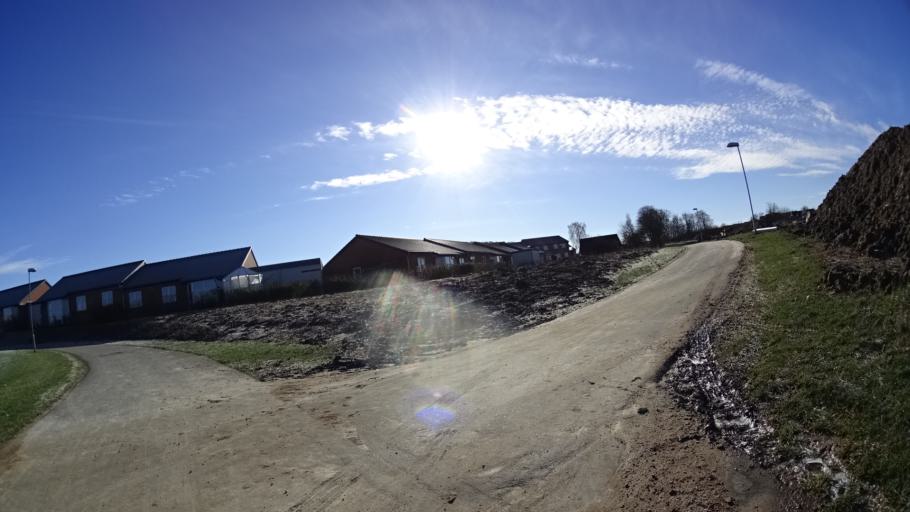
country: DK
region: Central Jutland
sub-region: Arhus Kommune
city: Kolt
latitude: 56.1149
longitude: 10.0872
